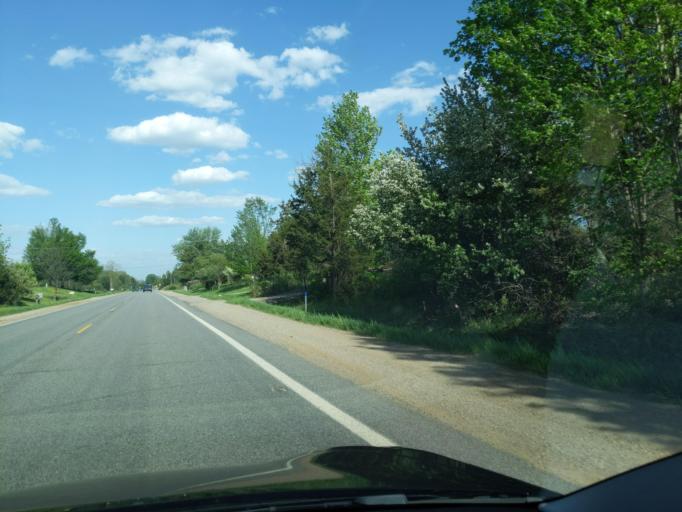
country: US
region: Michigan
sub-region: Eaton County
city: Grand Ledge
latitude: 42.7555
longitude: -84.7856
